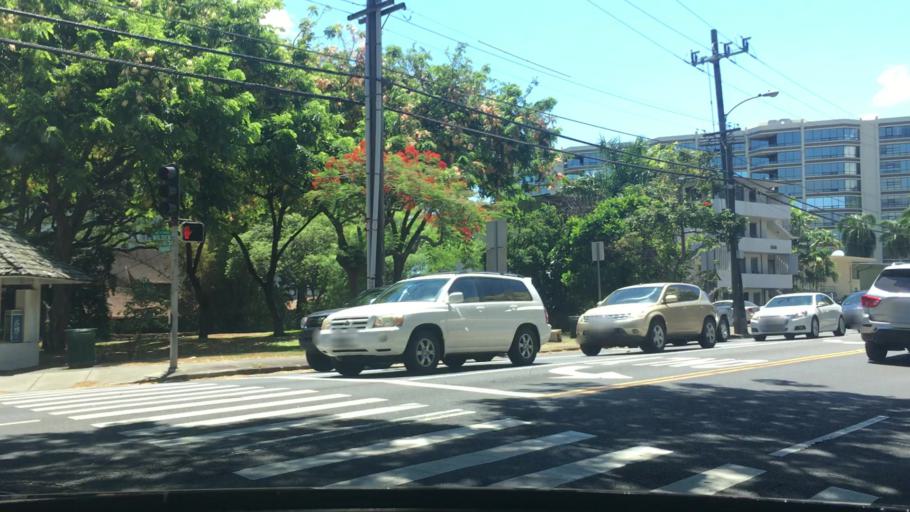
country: US
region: Hawaii
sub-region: Honolulu County
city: Honolulu
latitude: 21.3030
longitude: -157.8326
